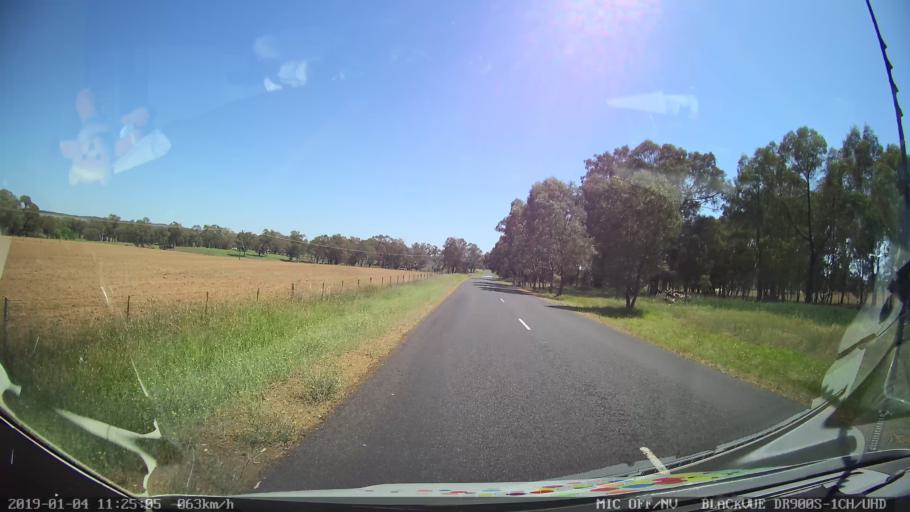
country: AU
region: New South Wales
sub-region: Cabonne
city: Molong
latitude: -33.1288
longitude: 148.7523
